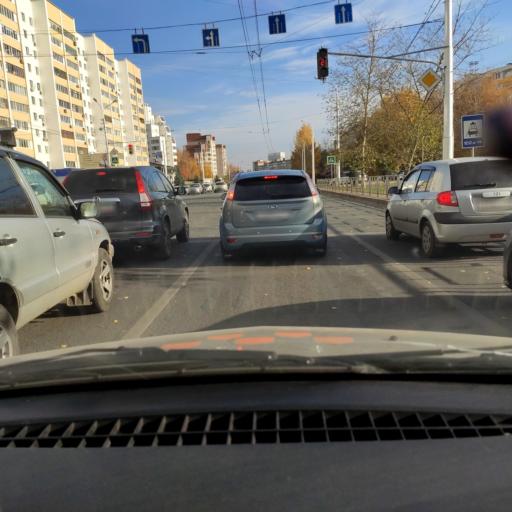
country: RU
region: Bashkortostan
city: Ufa
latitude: 54.7667
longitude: 56.0281
